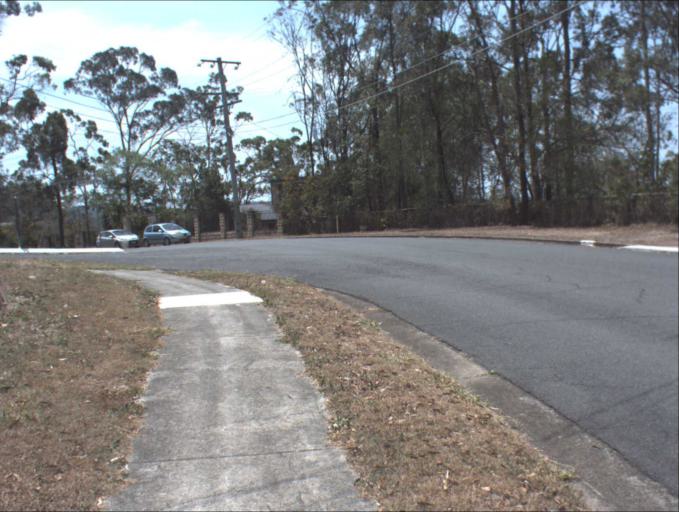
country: AU
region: Queensland
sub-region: Logan
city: Beenleigh
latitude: -27.6648
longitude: 153.1994
